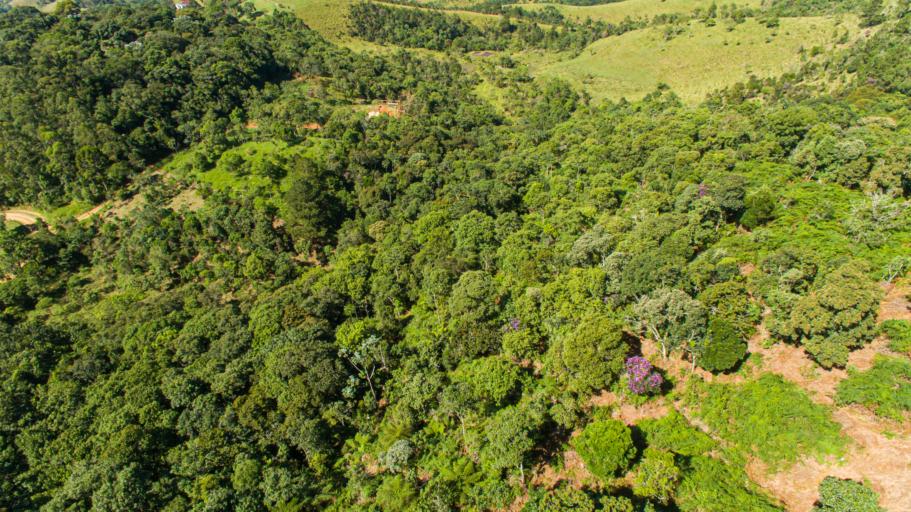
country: BR
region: Minas Gerais
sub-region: Camanducaia
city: Camanducaia
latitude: -22.8931
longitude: -45.9733
